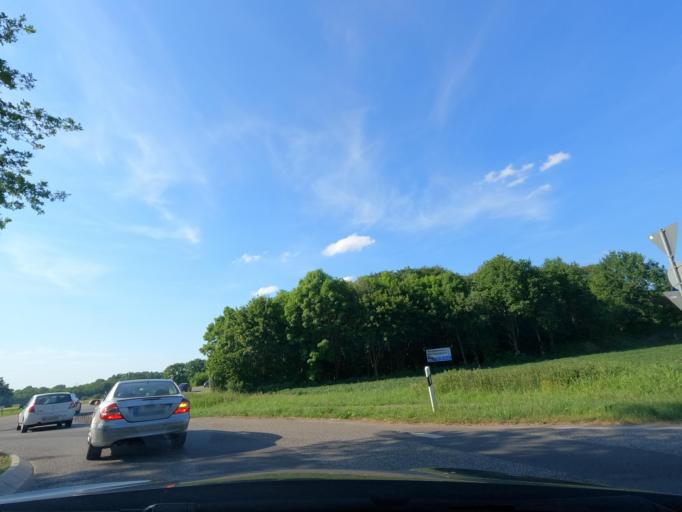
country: DE
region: Schleswig-Holstein
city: Klein Nordende
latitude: 53.7097
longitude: 9.6478
